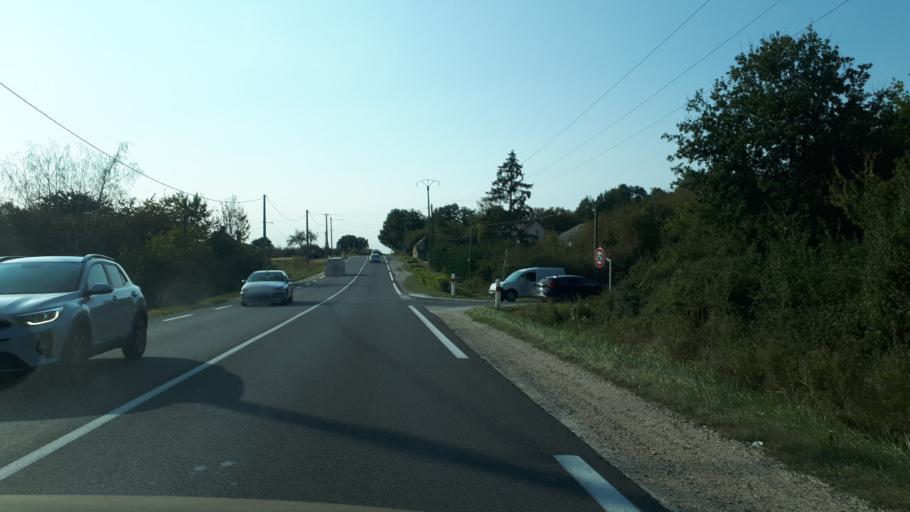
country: FR
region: Centre
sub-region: Departement du Cher
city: Vignoux-sur-Barangeon
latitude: 47.2073
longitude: 2.1520
